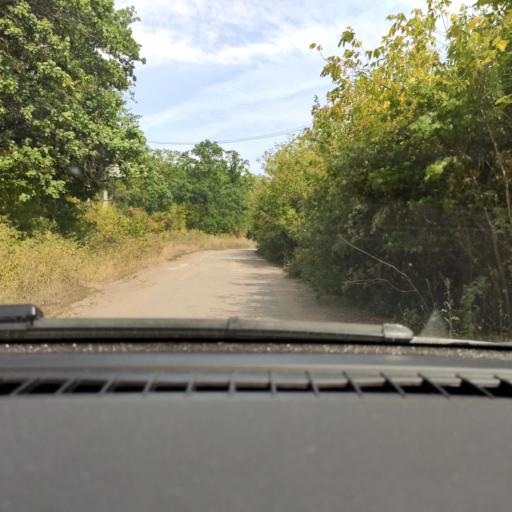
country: RU
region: Voronezj
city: Pridonskoy
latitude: 51.7503
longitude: 39.0763
